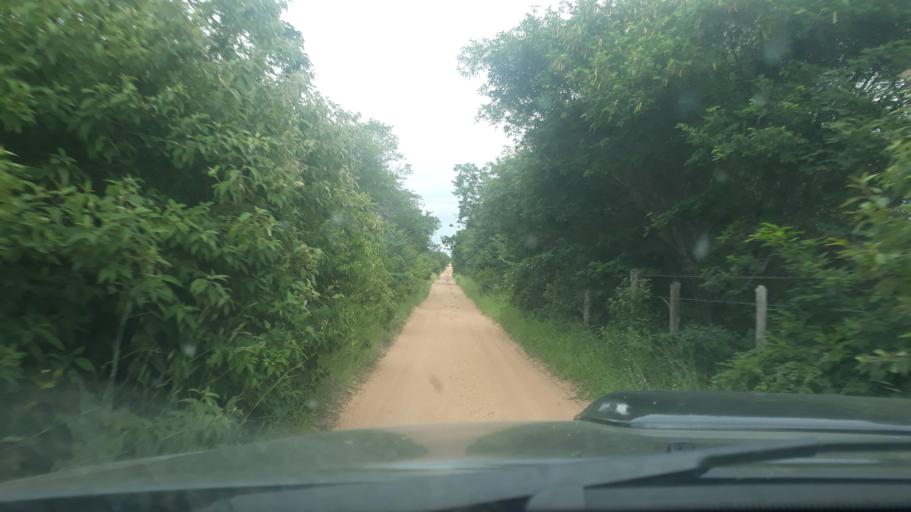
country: BR
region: Bahia
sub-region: Riacho De Santana
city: Riacho de Santana
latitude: -13.8582
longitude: -43.0405
